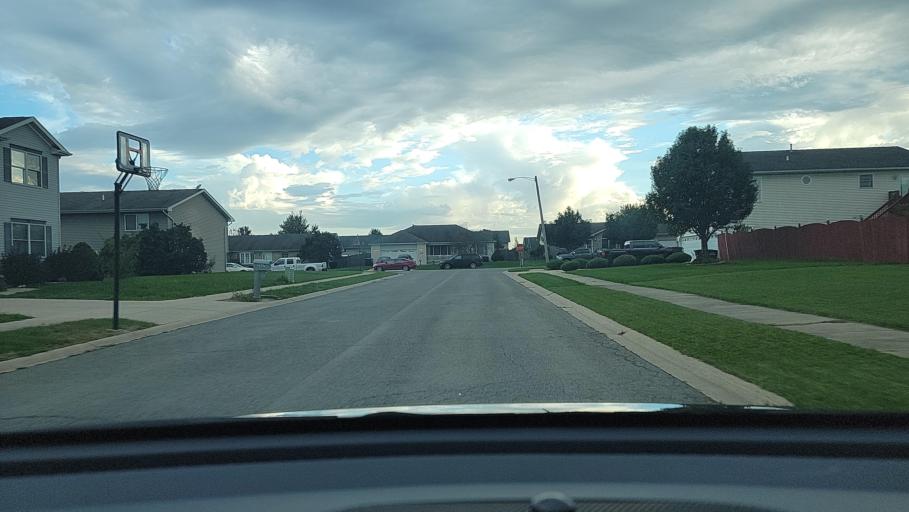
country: US
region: Indiana
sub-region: Porter County
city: Portage
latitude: 41.5661
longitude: -87.1607
